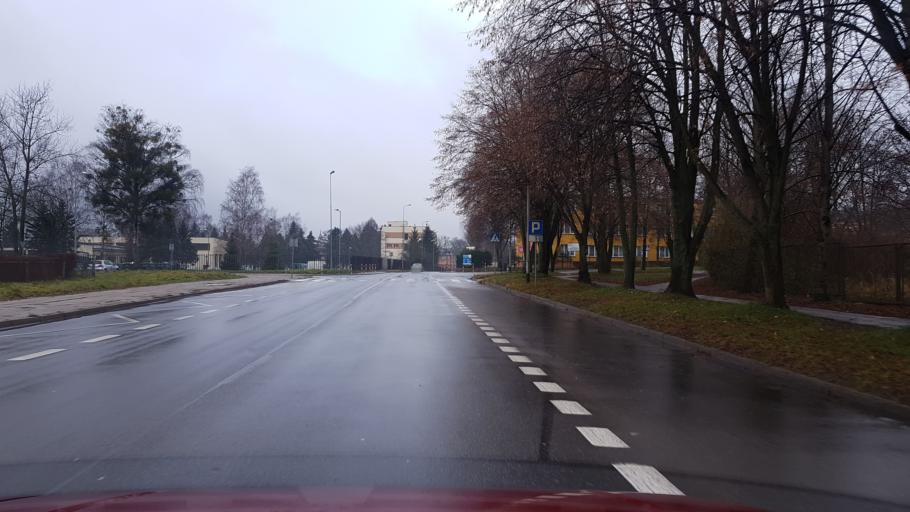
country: PL
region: West Pomeranian Voivodeship
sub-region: Koszalin
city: Koszalin
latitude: 54.1951
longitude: 16.2174
